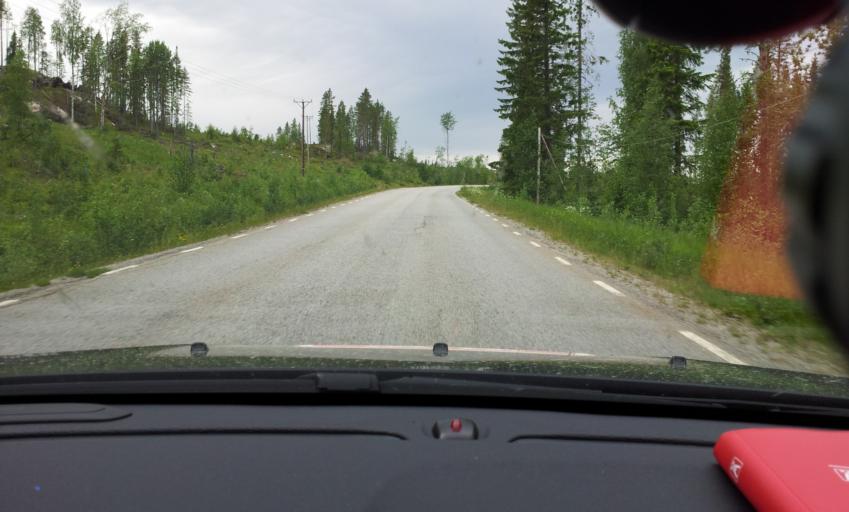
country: SE
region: Jaemtland
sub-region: Bergs Kommun
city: Hoverberg
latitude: 62.6688
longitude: 14.7240
